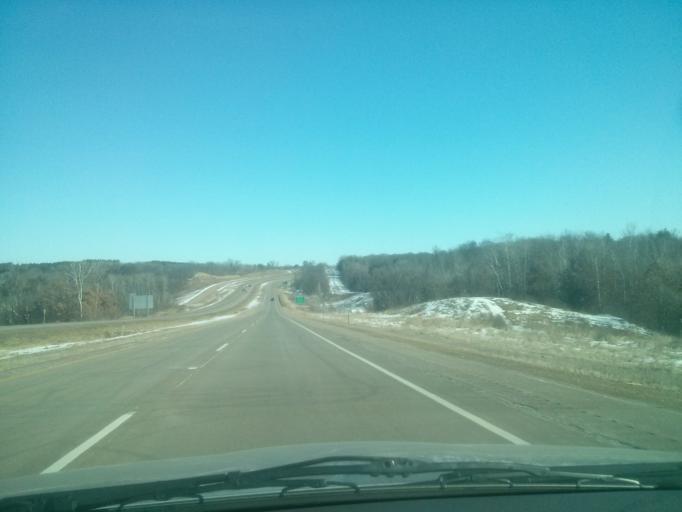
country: US
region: Wisconsin
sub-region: Saint Croix County
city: Somerset
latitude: 45.0978
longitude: -92.7341
